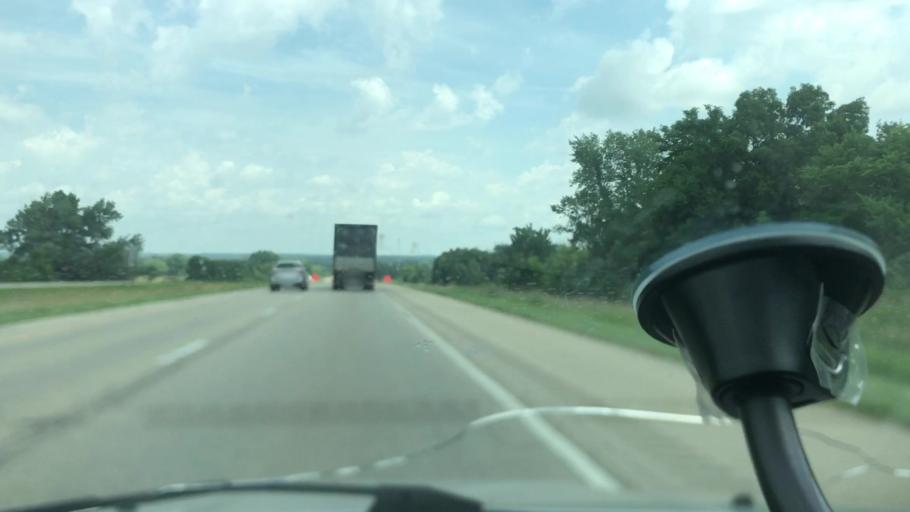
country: US
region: Illinois
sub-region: Peoria County
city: Bellevue
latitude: 40.7060
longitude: -89.6758
